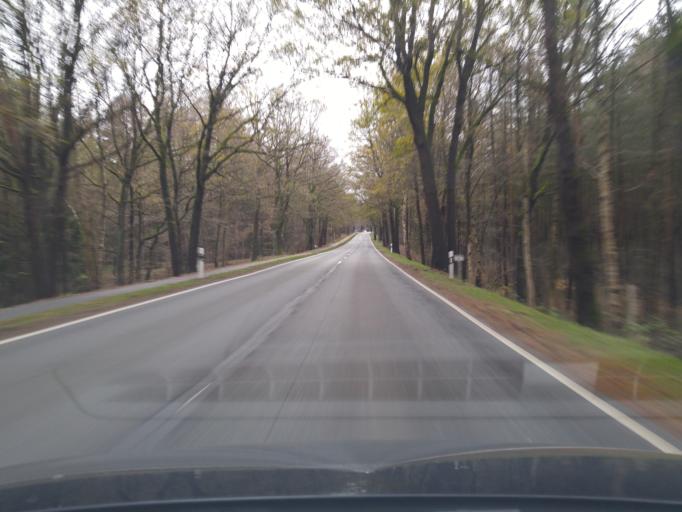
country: DE
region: Lower Saxony
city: Winsen
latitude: 52.7138
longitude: 9.9205
